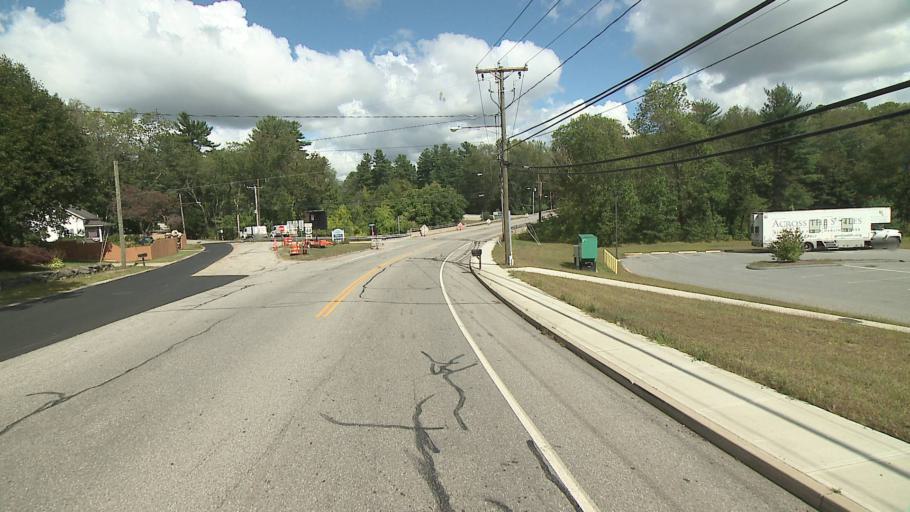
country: US
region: Connecticut
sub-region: Windham County
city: Putnam
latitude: 41.9113
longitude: -71.9160
